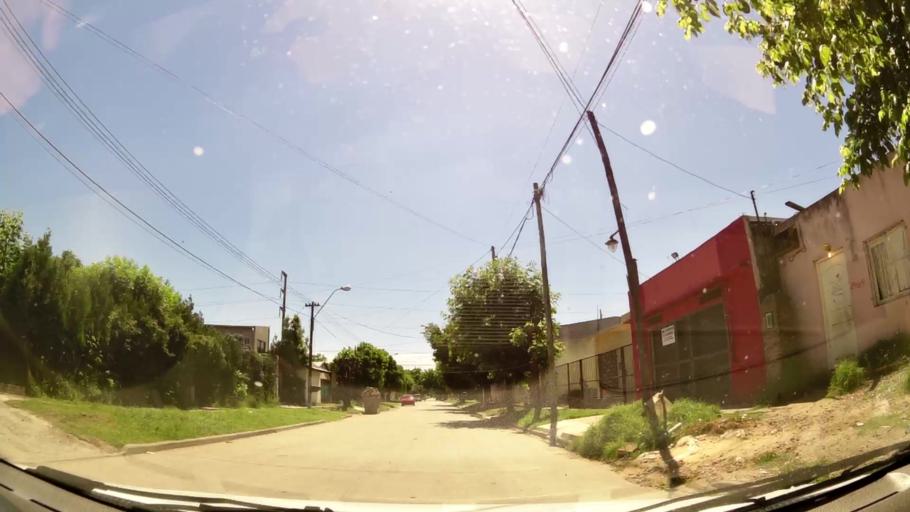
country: AR
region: Buenos Aires
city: Ituzaingo
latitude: -34.6786
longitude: -58.6754
